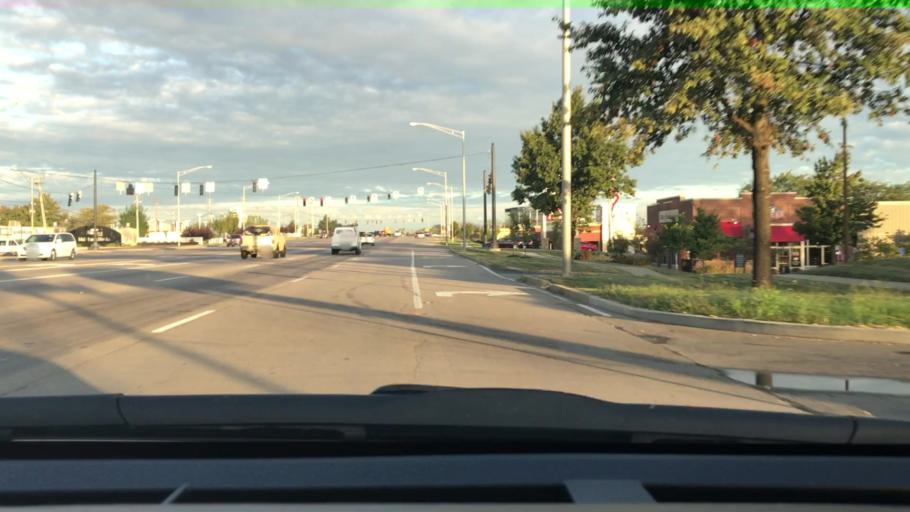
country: US
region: Kentucky
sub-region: Boone County
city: Florence
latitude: 39.0028
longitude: -84.6511
